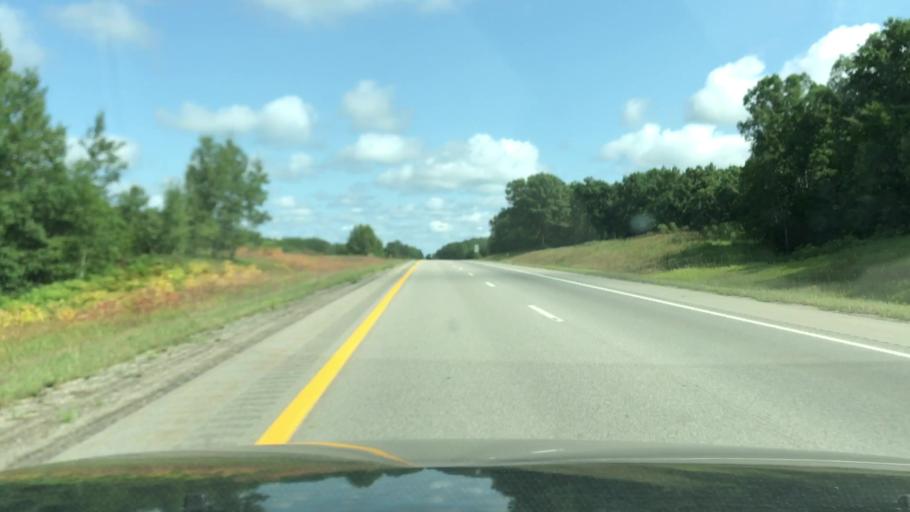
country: US
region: Michigan
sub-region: Montcalm County
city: Howard City
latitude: 43.5002
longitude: -85.4860
